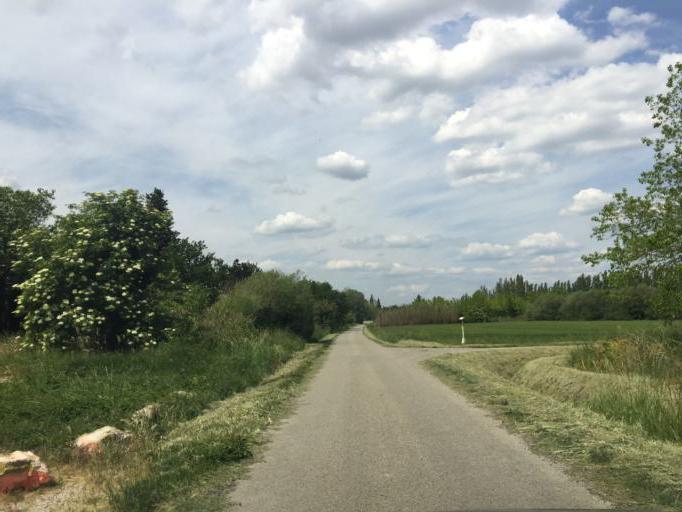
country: FR
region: Provence-Alpes-Cote d'Azur
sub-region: Departement du Vaucluse
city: Jonquieres
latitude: 44.1220
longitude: 4.8838
